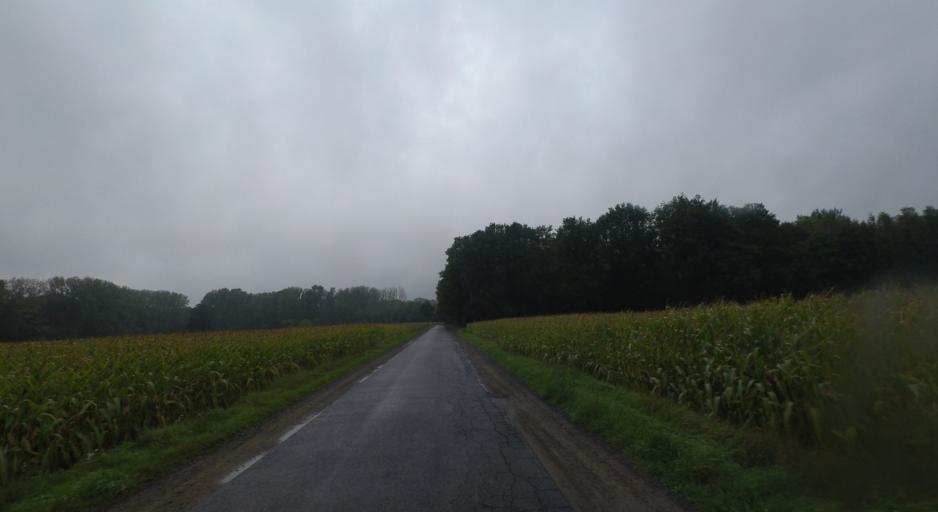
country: DE
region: North Rhine-Westphalia
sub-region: Regierungsbezirk Dusseldorf
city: Hamminkeln
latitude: 51.7103
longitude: 6.6167
